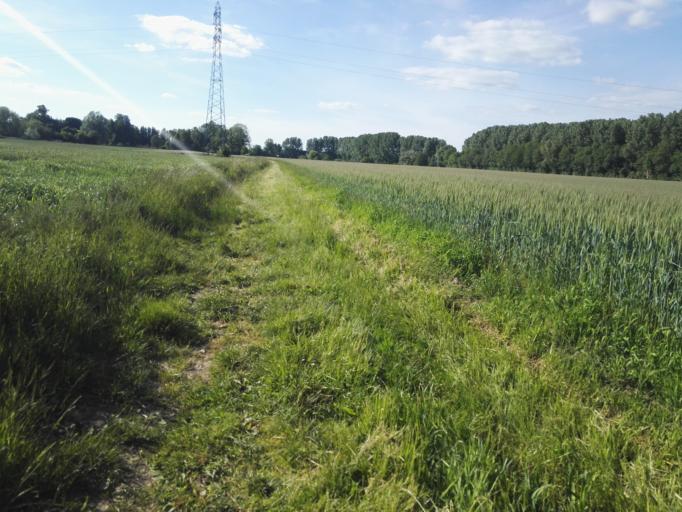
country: FR
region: Haute-Normandie
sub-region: Departement de l'Eure
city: Pacy-sur-Eure
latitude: 48.9926
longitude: 1.3948
